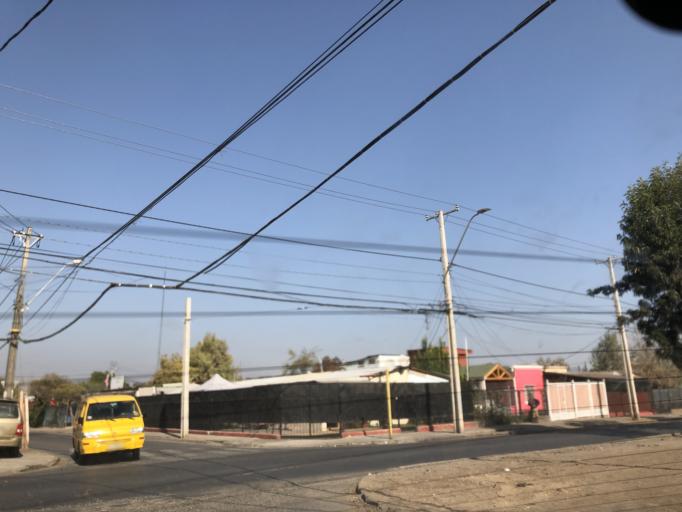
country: CL
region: Santiago Metropolitan
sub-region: Provincia de Cordillera
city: Puente Alto
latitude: -33.6145
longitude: -70.5812
